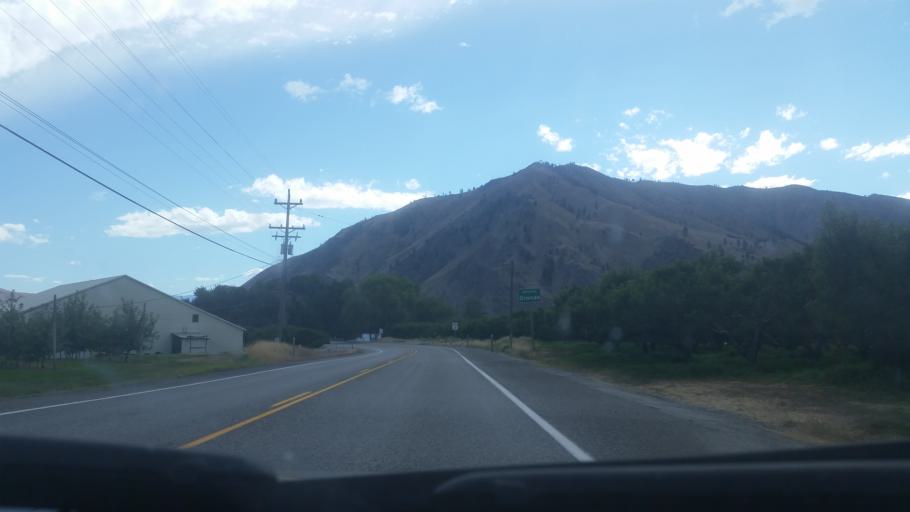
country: US
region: Washington
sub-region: Chelan County
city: Entiat
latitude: 47.6320
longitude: -120.2262
